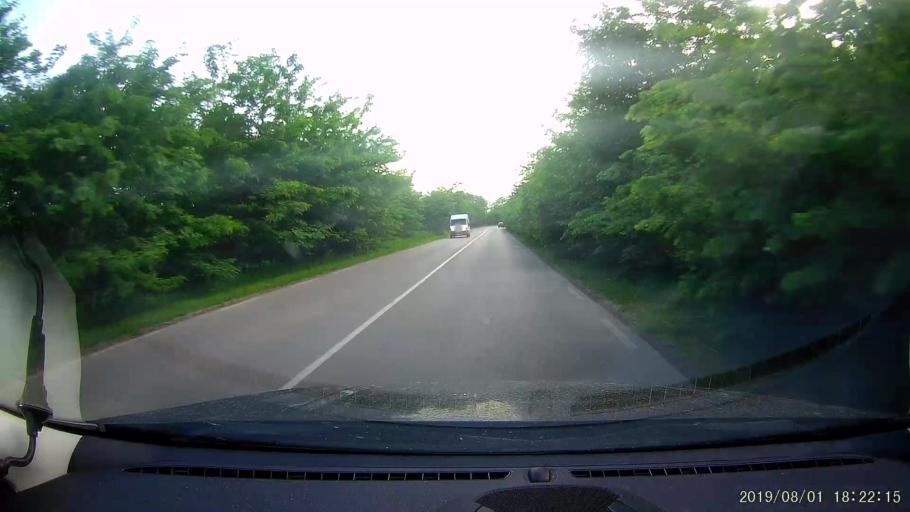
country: BG
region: Shumen
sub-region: Obshtina Kaolinovo
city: Kaolinovo
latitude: 43.6402
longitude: 27.0555
